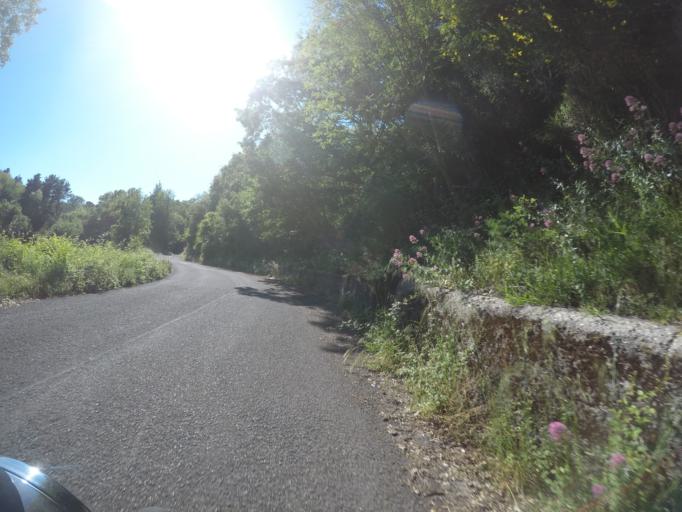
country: IT
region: Tuscany
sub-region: Provincia di Massa-Carrara
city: Fosdinovo
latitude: 44.1461
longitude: 10.0776
